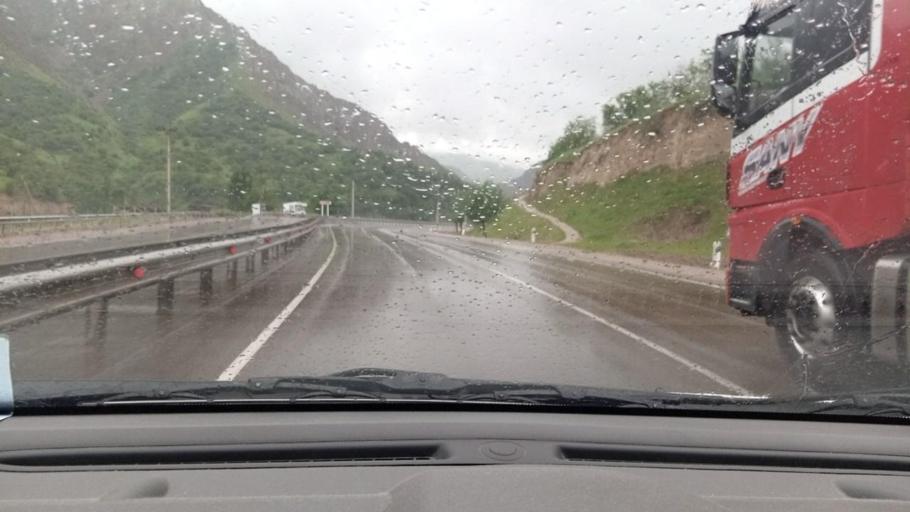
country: UZ
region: Toshkent
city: Angren
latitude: 41.1020
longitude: 70.3297
